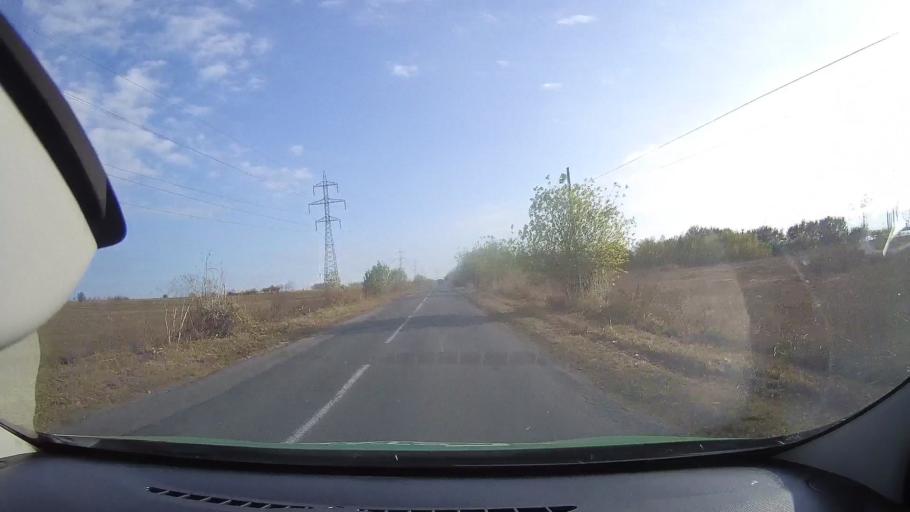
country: RO
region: Constanta
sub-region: Comuna Corbu
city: Corbu
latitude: 44.3735
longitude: 28.6648
